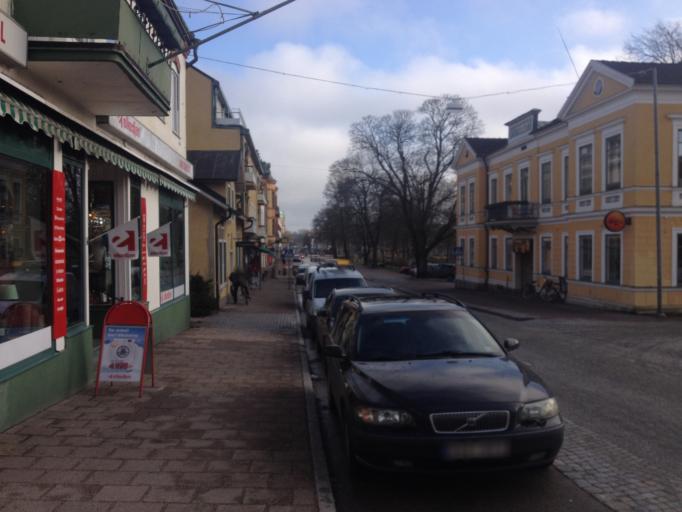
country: SE
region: Kronoberg
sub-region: Ljungby Kommun
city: Ljungby
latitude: 56.8339
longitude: 13.9370
